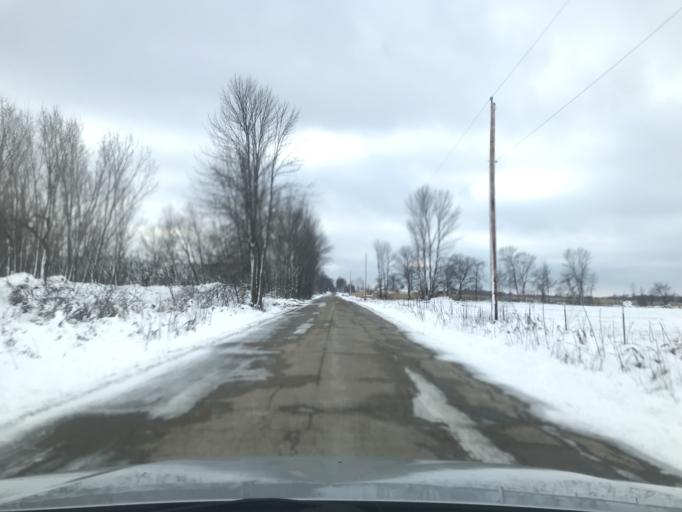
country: US
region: Wisconsin
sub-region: Oconto County
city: Oconto
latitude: 44.9307
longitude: -87.9922
